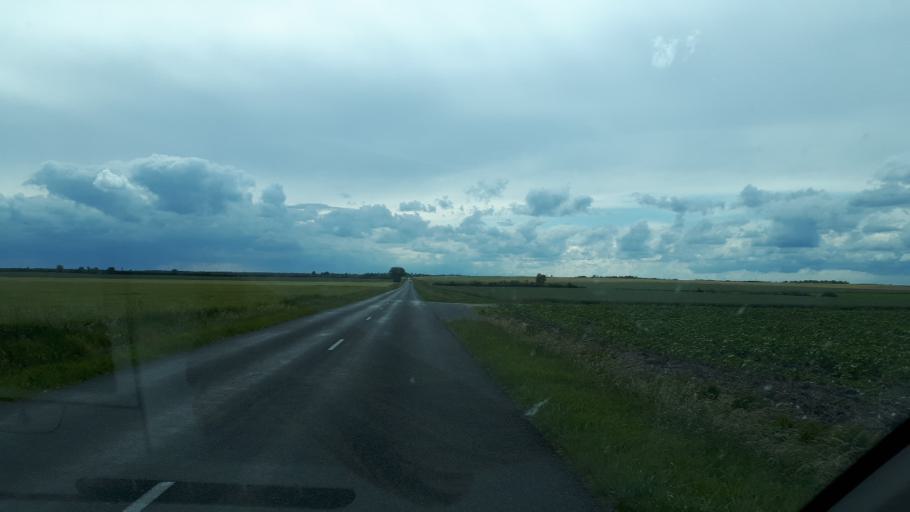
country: FR
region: Centre
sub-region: Departement du Cher
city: Marmagne
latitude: 47.0813
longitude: 2.2317
